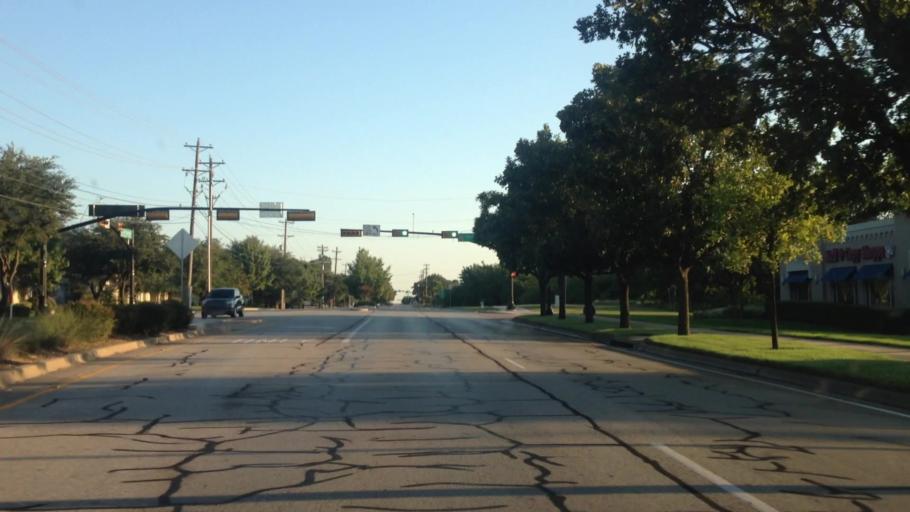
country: US
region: Texas
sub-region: Tarrant County
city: Southlake
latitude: 32.9449
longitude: -97.1341
